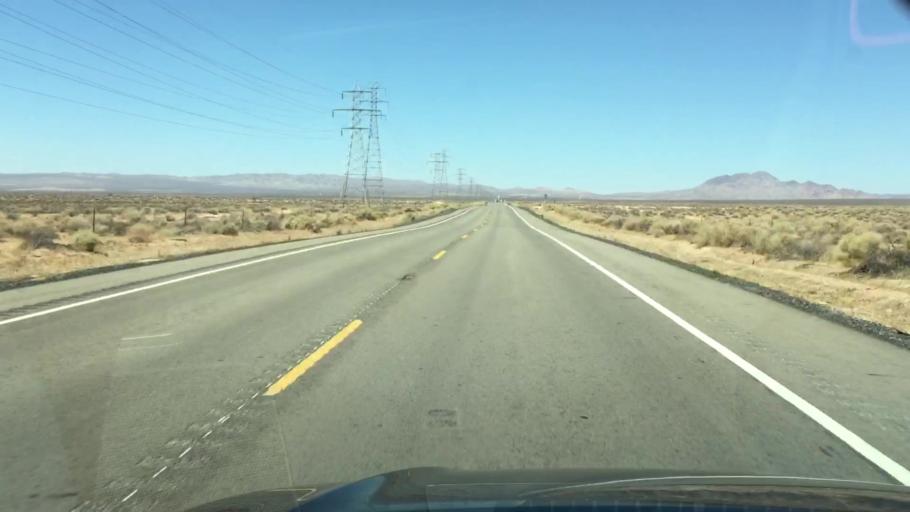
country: US
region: California
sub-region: Kern County
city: Boron
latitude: 35.1734
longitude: -117.5921
